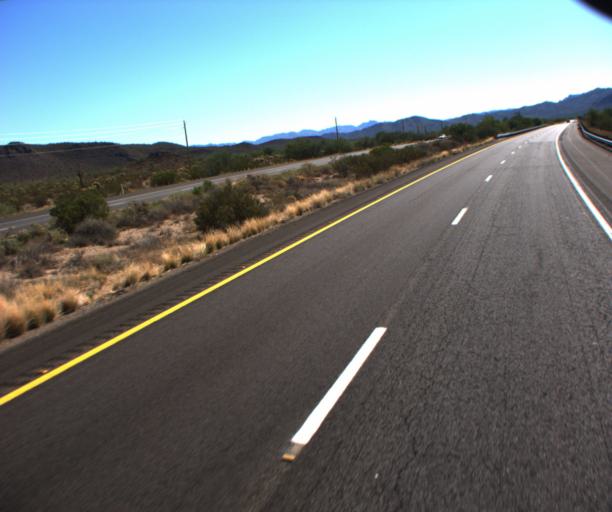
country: US
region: Arizona
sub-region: Pinal County
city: Gold Camp
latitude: 33.2572
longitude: -111.3237
